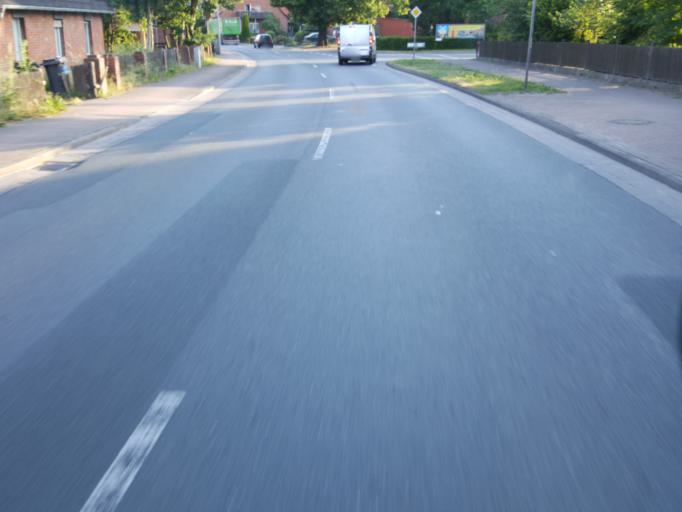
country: DE
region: Lower Saxony
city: Landesbergen
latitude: 52.5536
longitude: 9.1198
